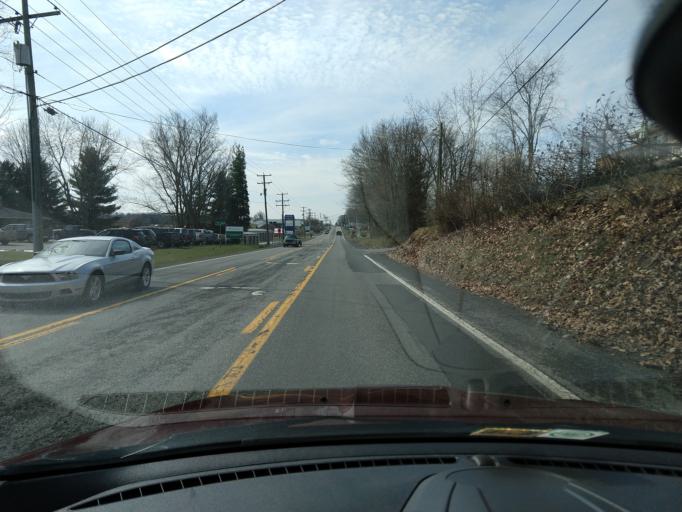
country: US
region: West Virginia
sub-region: Greenbrier County
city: Lewisburg
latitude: 37.8368
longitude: -80.4164
